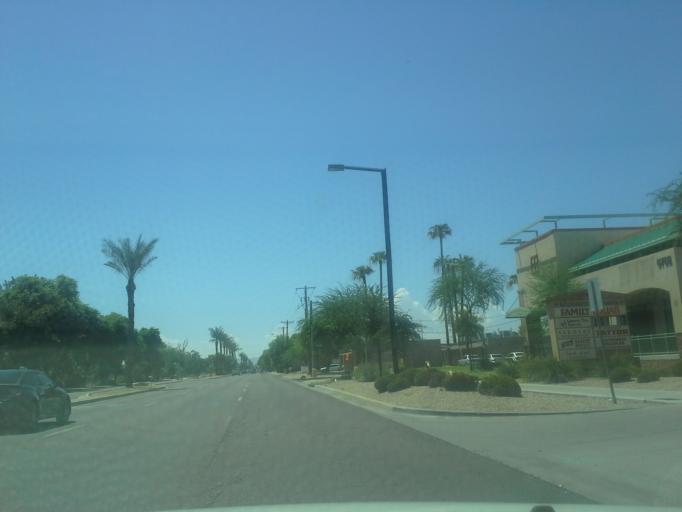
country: US
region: Arizona
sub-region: Maricopa County
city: Glendale
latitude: 33.5384
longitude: -112.2044
